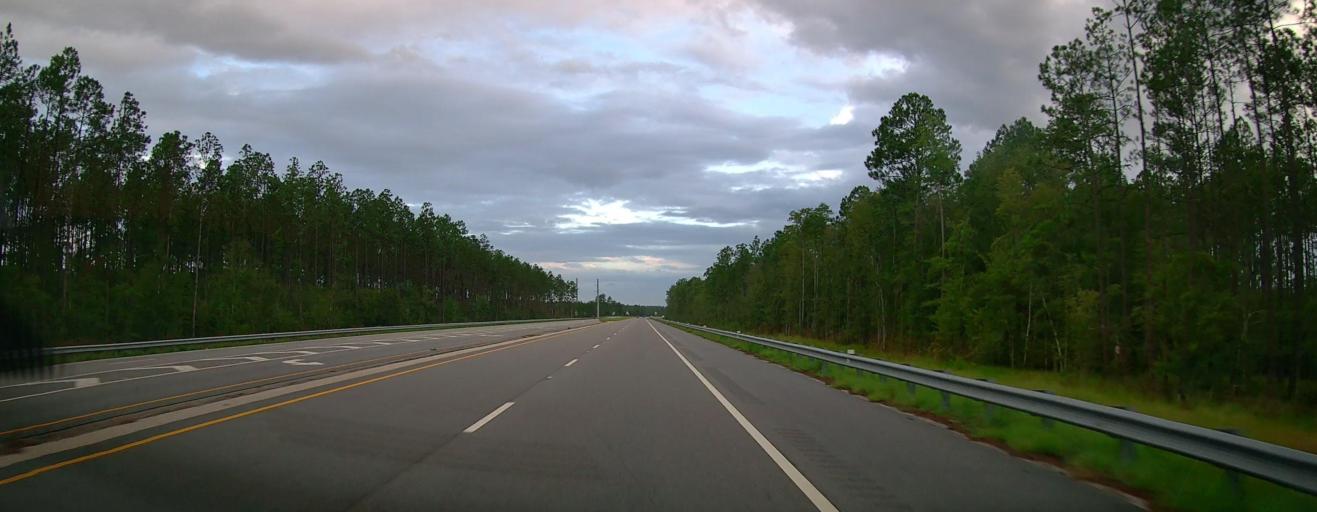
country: US
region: Georgia
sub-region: Ware County
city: Deenwood
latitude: 31.1729
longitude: -82.4086
